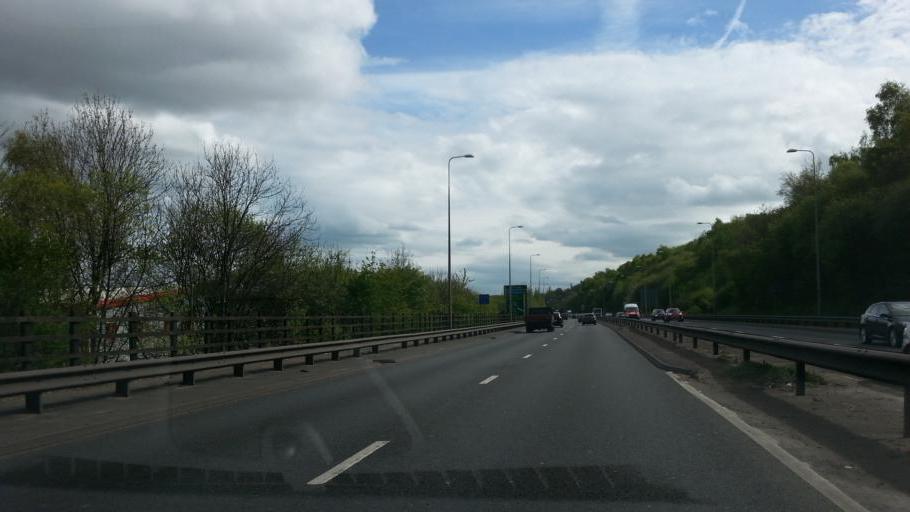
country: GB
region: England
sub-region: Stoke-on-Trent
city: Stoke-on-Trent
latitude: 53.0272
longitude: -2.2073
